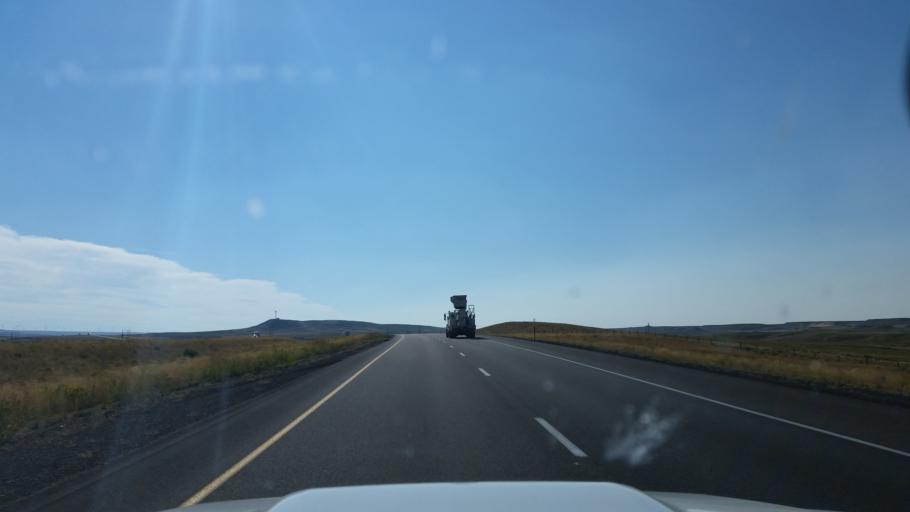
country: US
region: Wyoming
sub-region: Uinta County
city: Lyman
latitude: 41.3549
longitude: -110.3642
